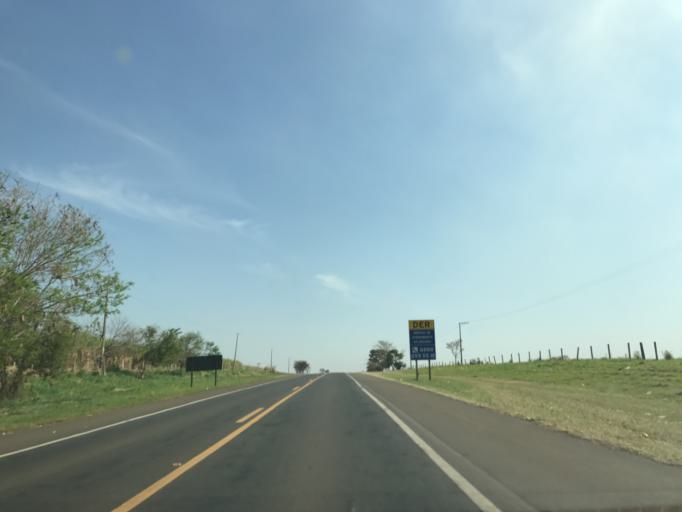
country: BR
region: Sao Paulo
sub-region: Penapolis
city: Penapolis
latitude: -21.4065
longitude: -50.1152
